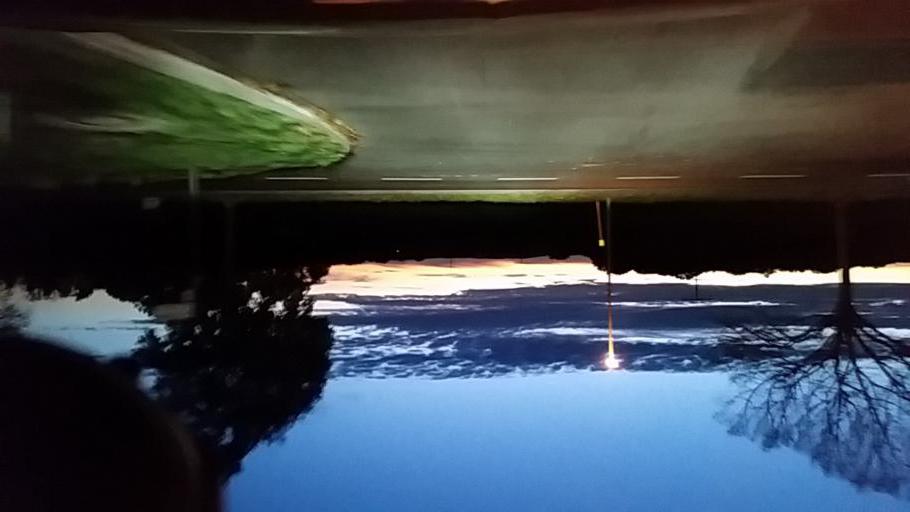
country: DE
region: Lower Saxony
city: Tappenbeck
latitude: 52.4741
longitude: 10.7622
